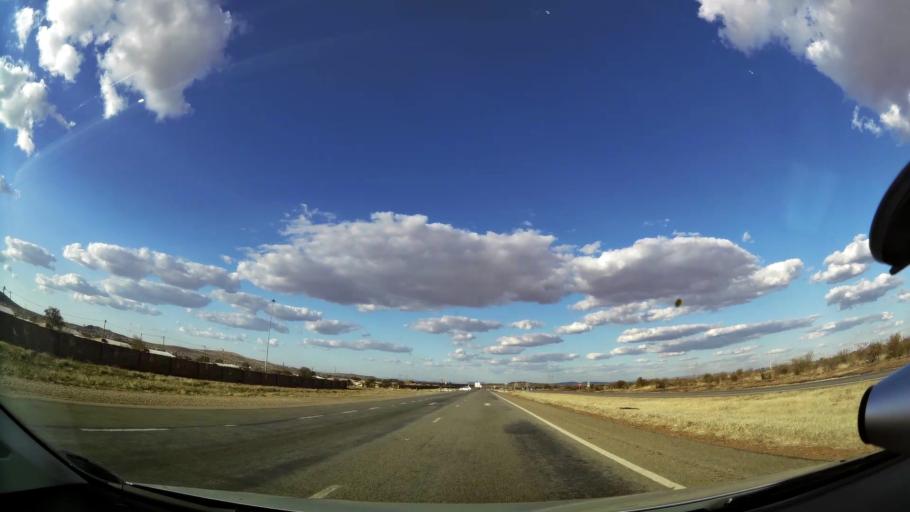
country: ZA
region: North-West
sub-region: Dr Kenneth Kaunda District Municipality
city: Potchefstroom
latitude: -26.7540
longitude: 27.0072
